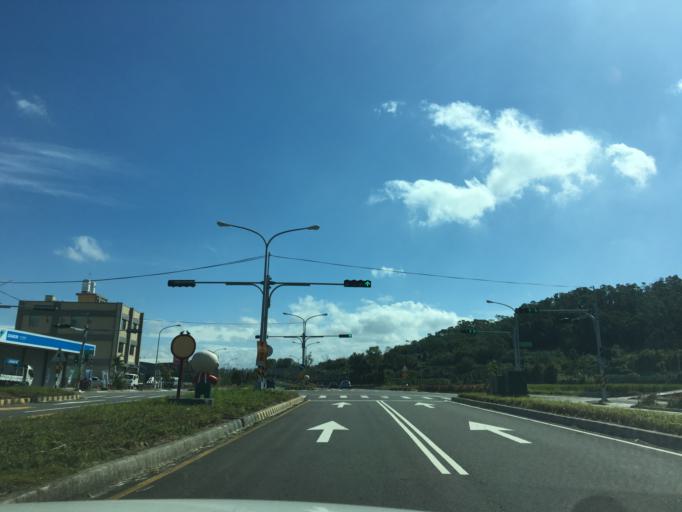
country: TW
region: Taiwan
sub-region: Hsinchu
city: Zhubei
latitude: 24.7817
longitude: 121.0425
